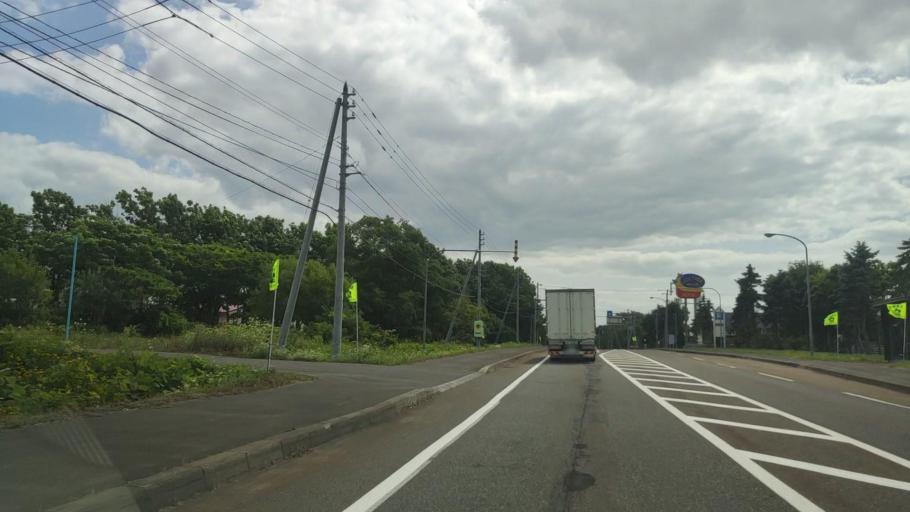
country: JP
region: Hokkaido
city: Rumoi
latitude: 44.5636
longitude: 141.7859
